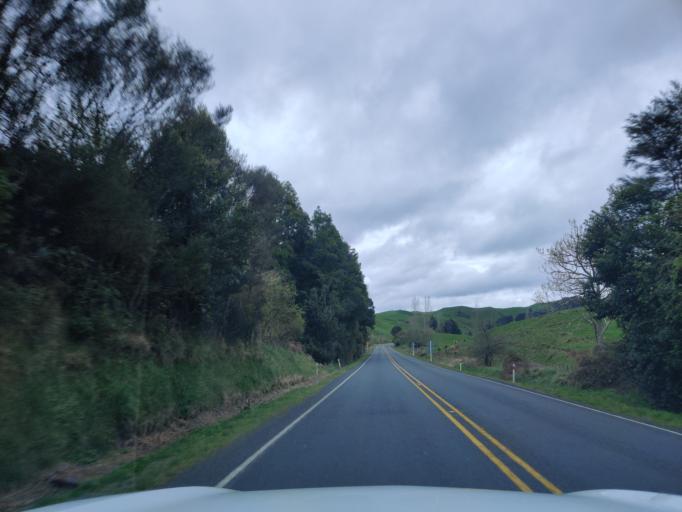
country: NZ
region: Waikato
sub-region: Otorohanga District
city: Otorohanga
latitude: -38.5273
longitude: 175.1755
